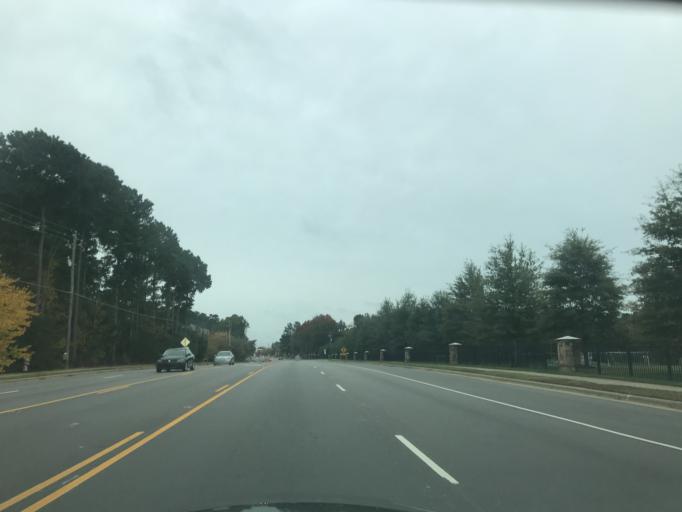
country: US
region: North Carolina
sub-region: Wake County
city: West Raleigh
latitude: 35.8847
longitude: -78.6270
